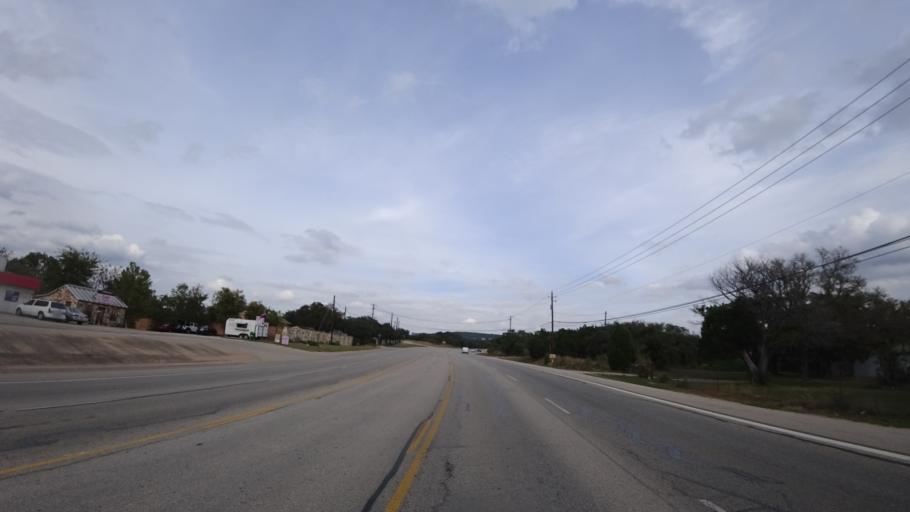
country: US
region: Texas
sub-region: Travis County
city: Hudson Bend
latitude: 30.3892
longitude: -97.8907
